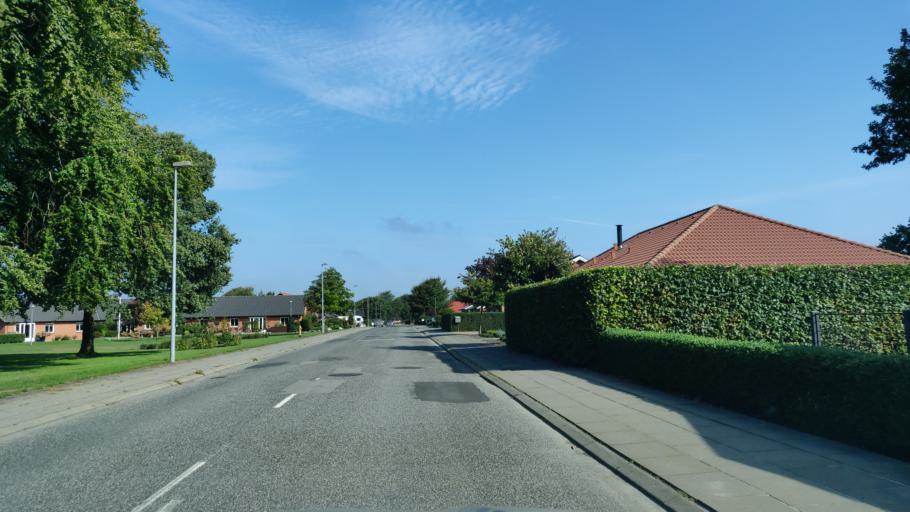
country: DK
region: Central Jutland
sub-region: Herning Kommune
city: Avlum
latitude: 56.2147
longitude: 8.8522
